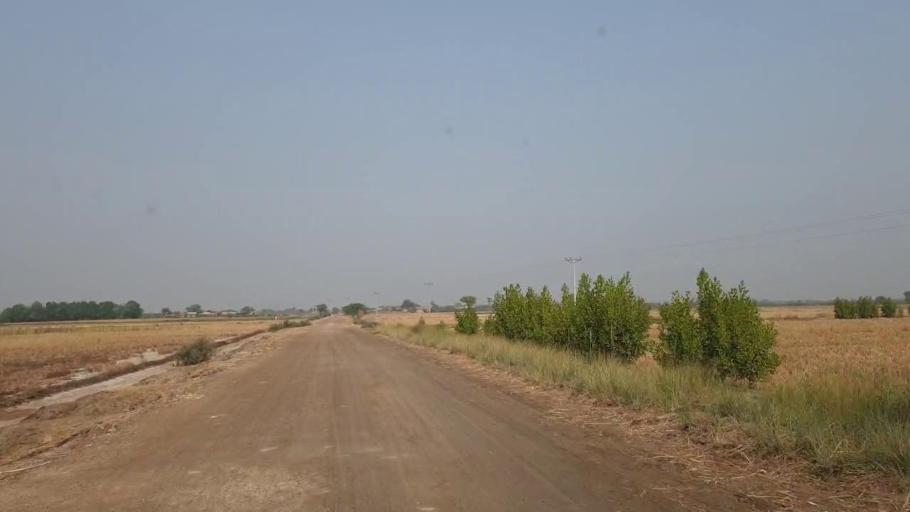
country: PK
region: Sindh
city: Matli
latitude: 25.1513
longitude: 68.7295
